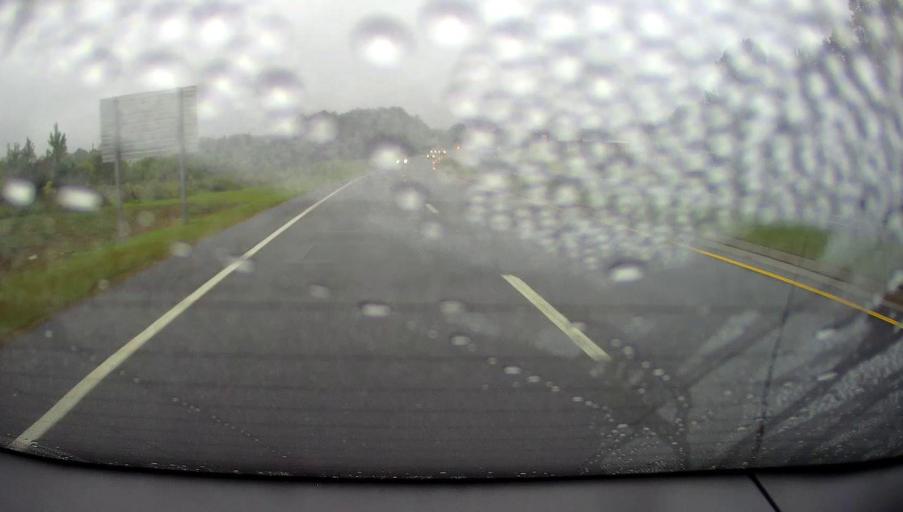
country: US
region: Georgia
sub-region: Houston County
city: Robins Air Force Base
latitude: 32.5512
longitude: -83.6012
